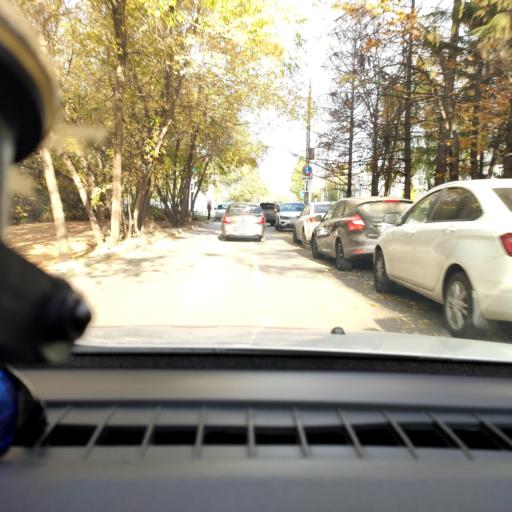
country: RU
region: Samara
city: Samara
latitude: 53.2133
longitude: 50.1863
